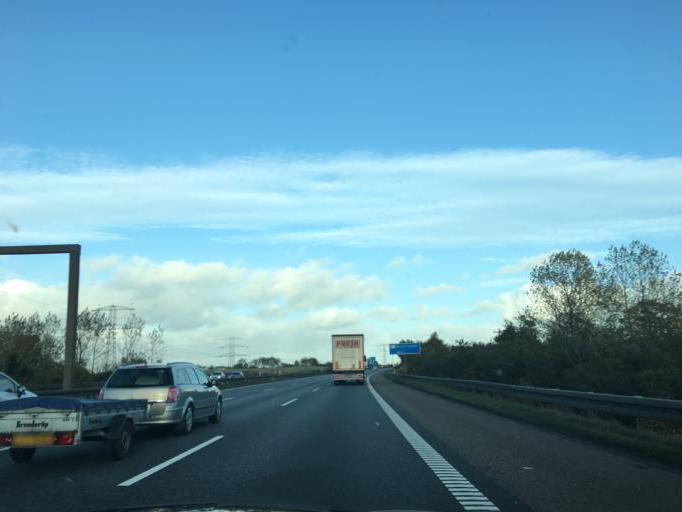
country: DK
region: South Denmark
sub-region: Kolding Kommune
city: Kolding
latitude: 55.5255
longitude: 9.4513
